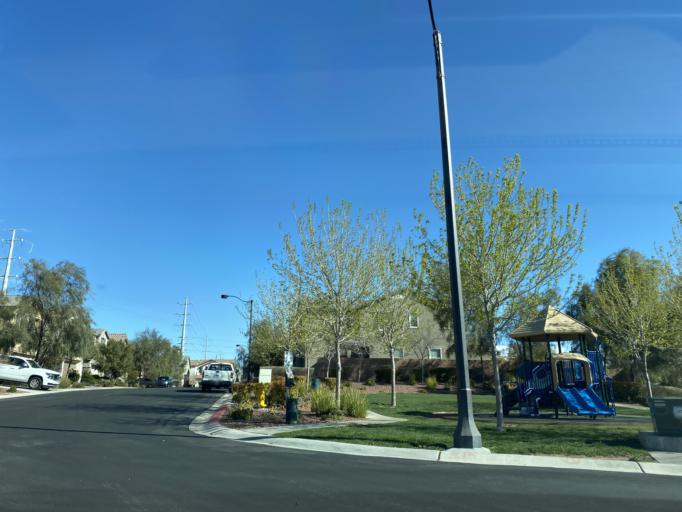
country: US
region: Nevada
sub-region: Clark County
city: Summerlin South
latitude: 36.3041
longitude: -115.3329
